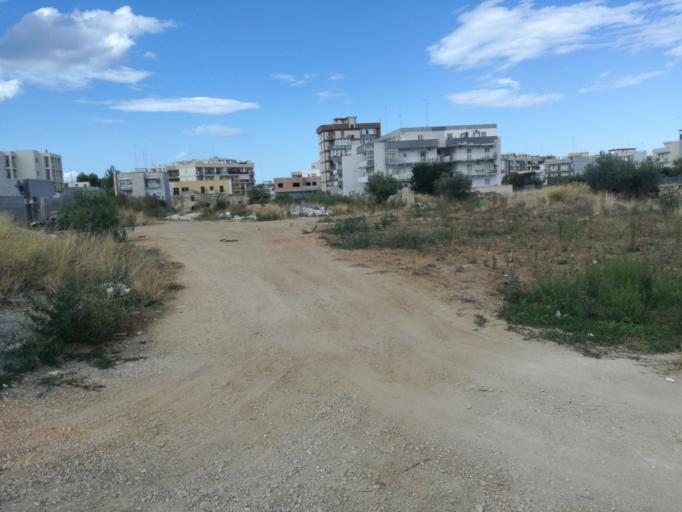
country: IT
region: Apulia
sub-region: Provincia di Bari
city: Triggiano
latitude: 41.0649
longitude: 16.9317
